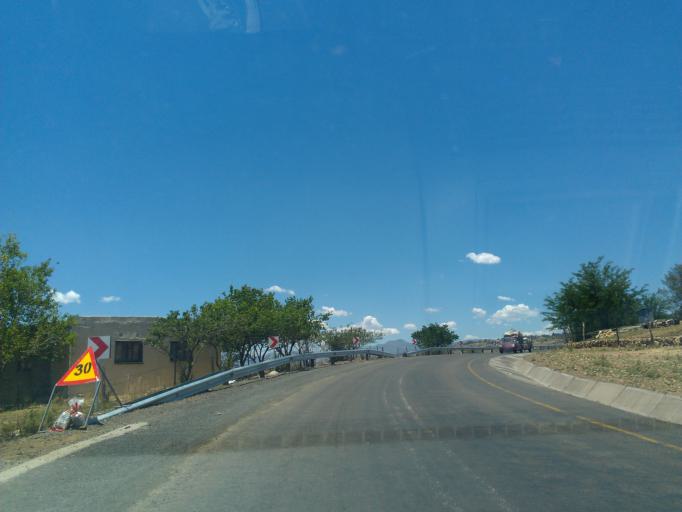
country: LS
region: Leribe
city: Maputsoe
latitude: -29.0907
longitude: 27.9618
